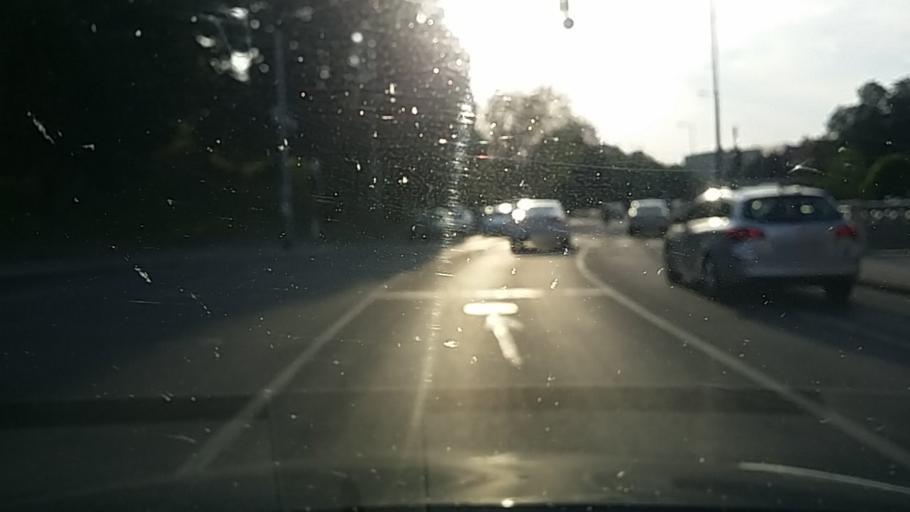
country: HU
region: Borsod-Abauj-Zemplen
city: Miskolc
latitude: 48.1019
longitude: 20.7796
